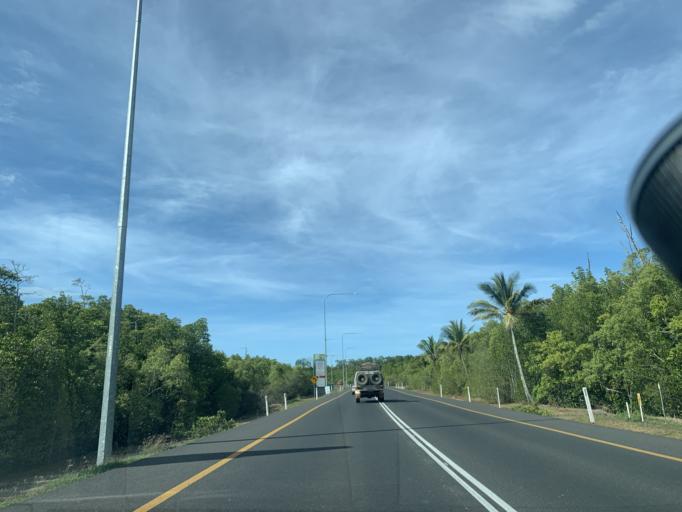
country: AU
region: Queensland
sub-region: Cairns
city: Cairns
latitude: -16.8899
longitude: 145.7614
